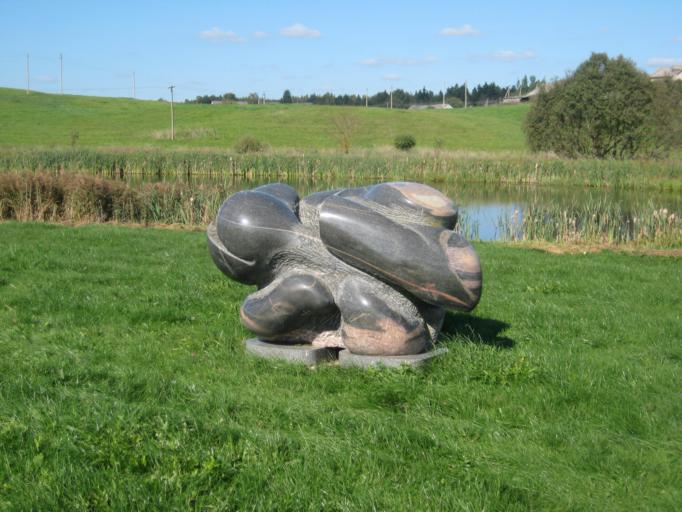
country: LT
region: Utenos apskritis
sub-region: Utena
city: Utena
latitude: 55.5471
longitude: 25.6135
